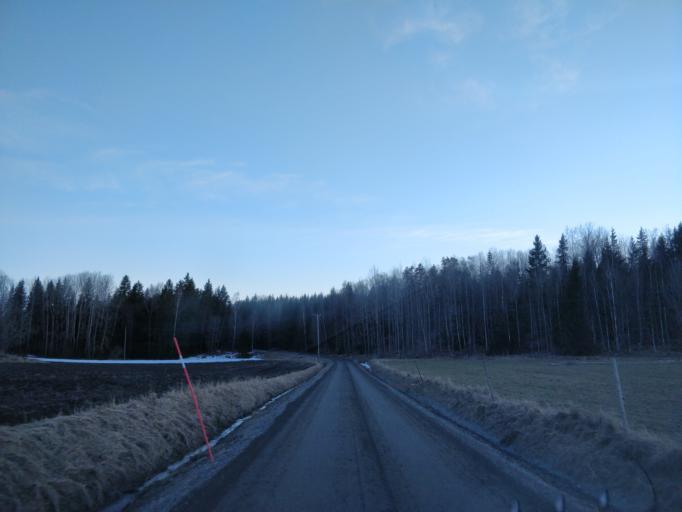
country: SE
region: Uppsala
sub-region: Enkopings Kommun
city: Orsundsbro
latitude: 59.8332
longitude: 17.1856
